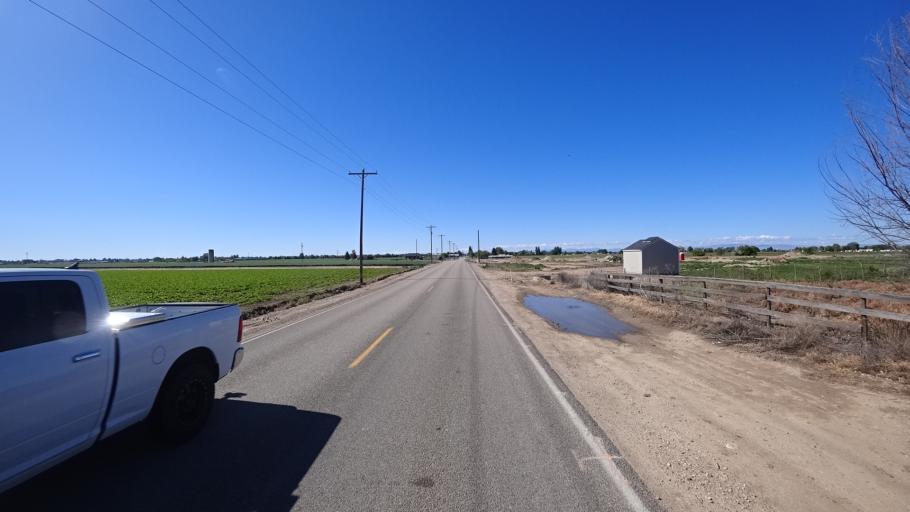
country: US
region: Idaho
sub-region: Ada County
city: Star
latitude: 43.6458
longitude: -116.4536
